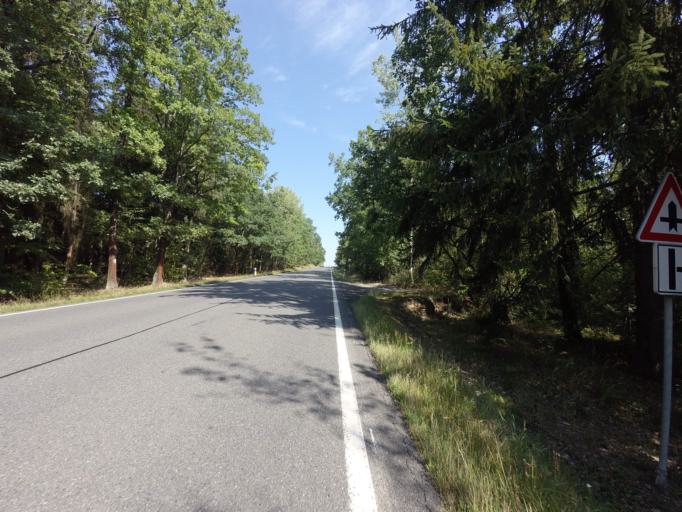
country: CZ
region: Jihocesky
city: Milevsko
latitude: 49.4244
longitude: 14.3591
